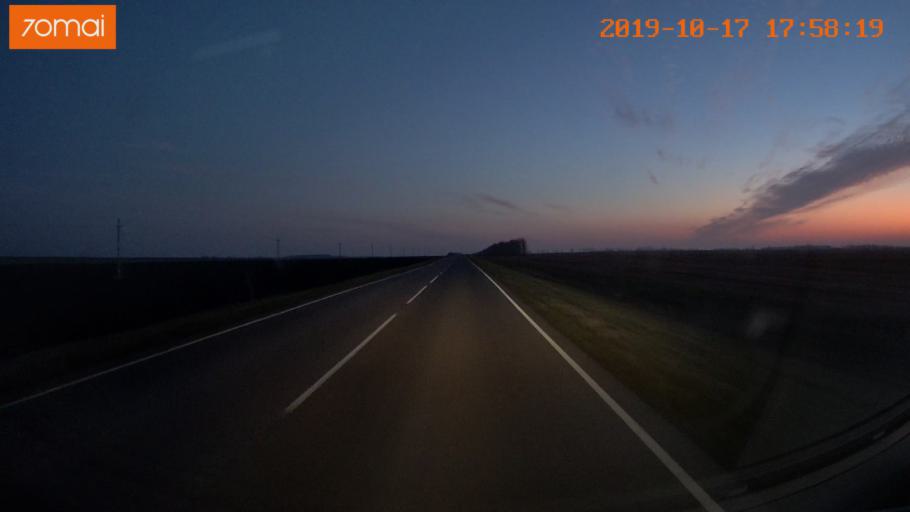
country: RU
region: Tula
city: Kurkino
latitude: 53.5568
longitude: 38.6283
